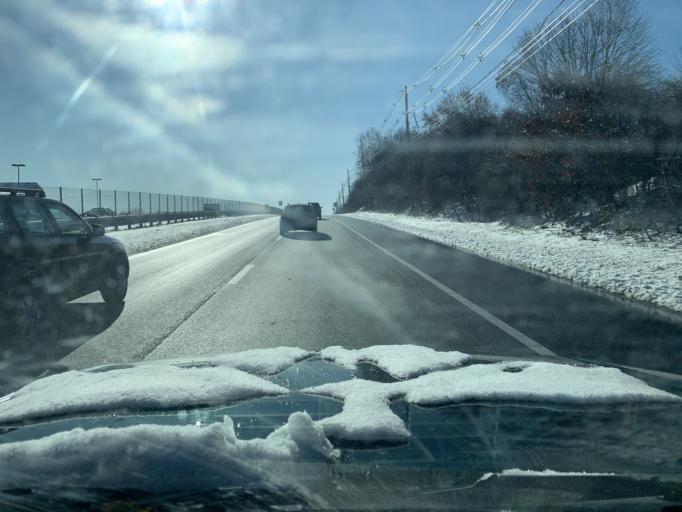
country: US
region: Massachusetts
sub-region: Essex County
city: Danvers
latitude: 42.5803
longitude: -70.9688
